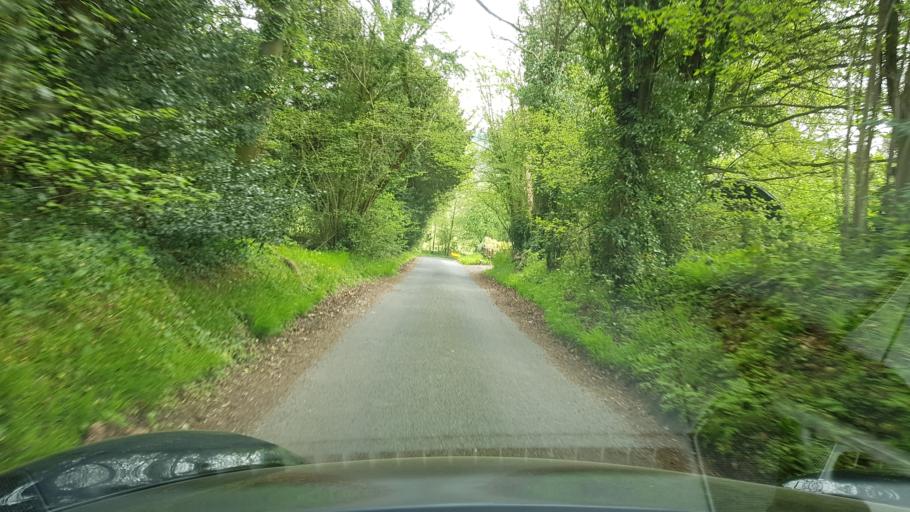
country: GB
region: England
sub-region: Surrey
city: East Horsley
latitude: 51.2466
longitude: -0.4480
